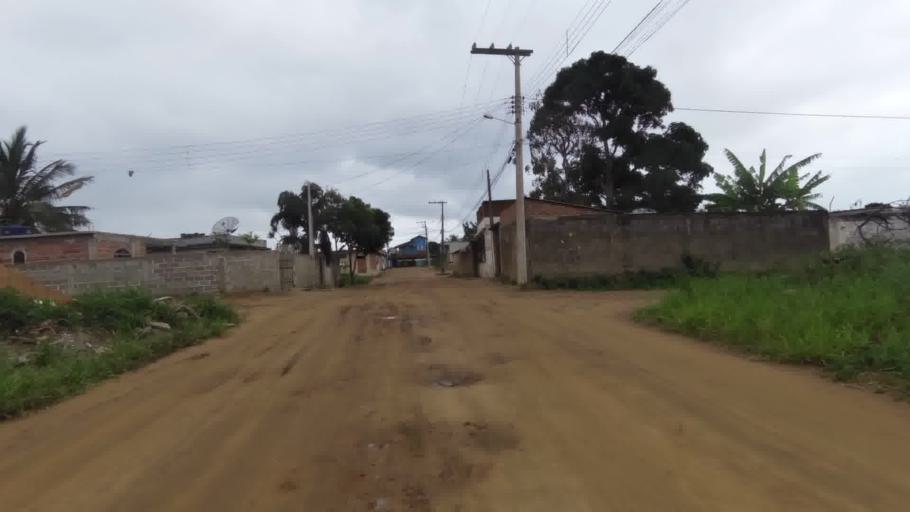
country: BR
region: Espirito Santo
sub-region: Marataizes
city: Marataizes
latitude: -21.0493
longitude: -40.8389
